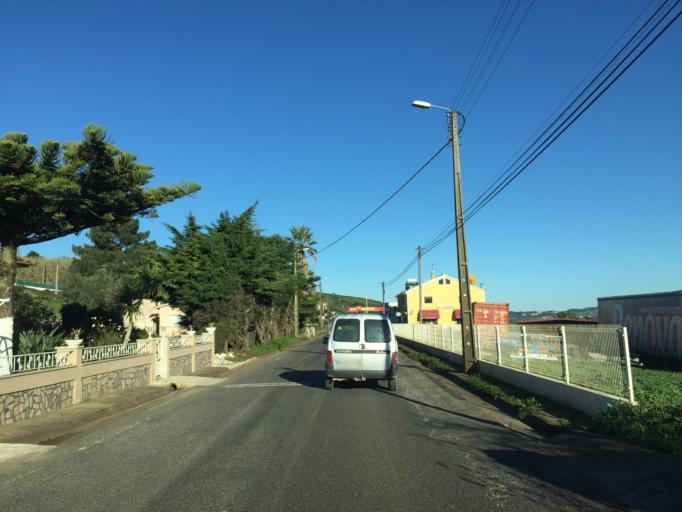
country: PT
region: Lisbon
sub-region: Sintra
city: Almargem
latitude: 38.8467
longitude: -9.2615
